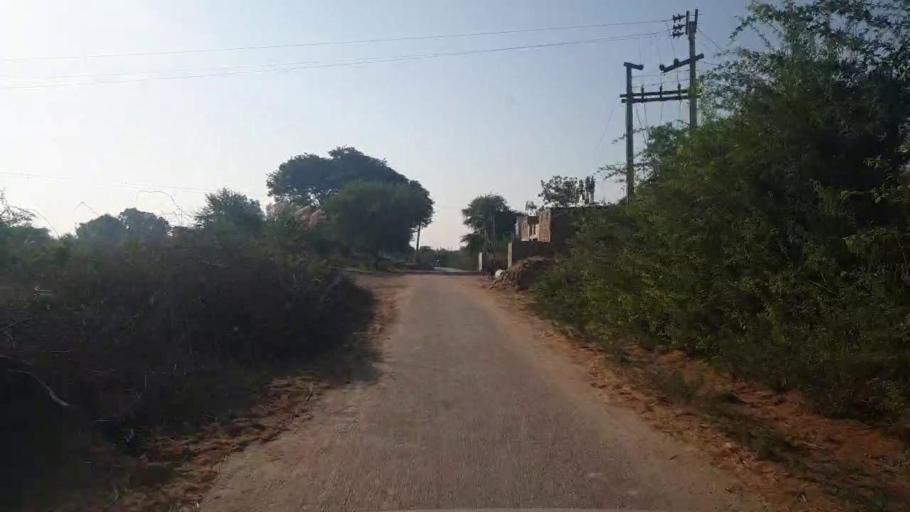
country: PK
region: Sindh
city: Tando Bago
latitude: 24.7365
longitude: 68.9308
